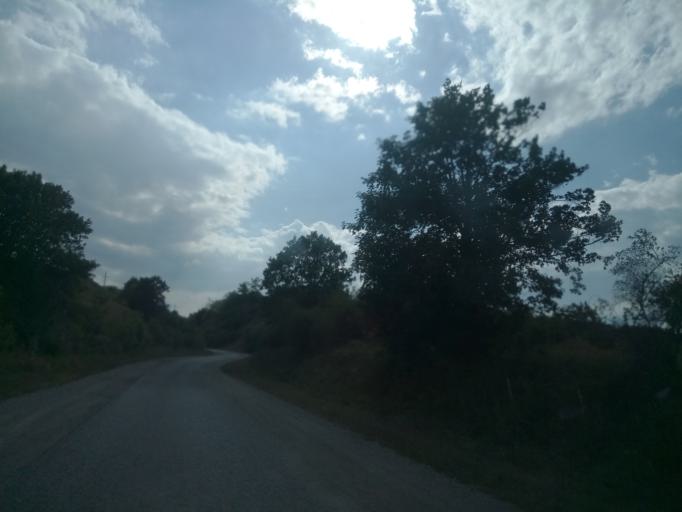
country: RS
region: Autonomna Pokrajina Vojvodina
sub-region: Sremski Okrug
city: Irig
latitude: 45.1034
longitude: 19.9059
